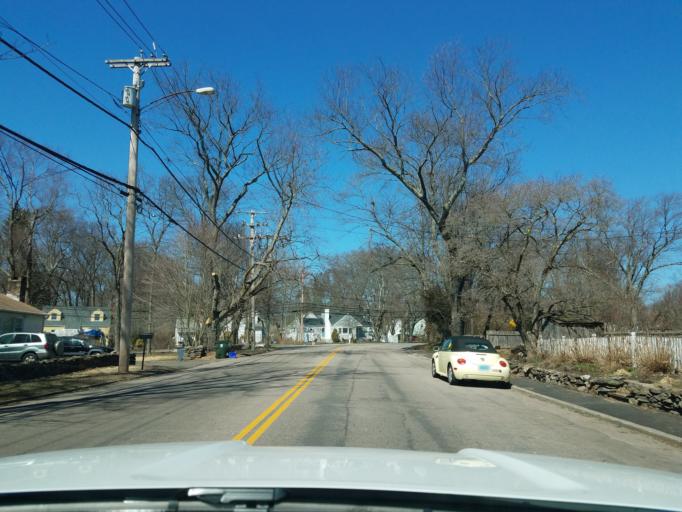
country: US
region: Connecticut
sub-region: Fairfield County
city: Fairfield
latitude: 41.1857
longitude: -73.2514
